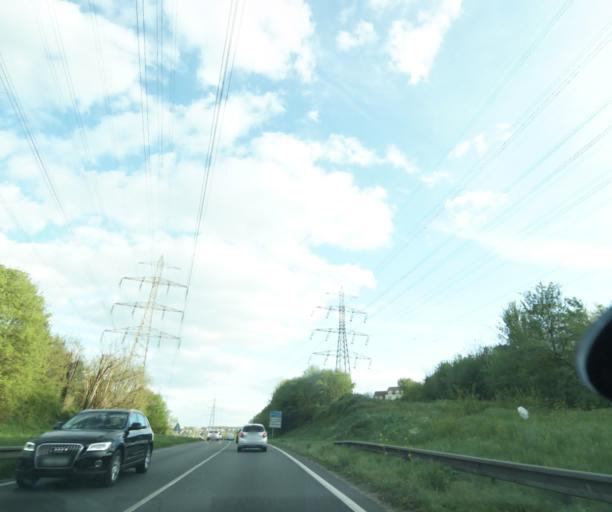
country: FR
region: Ile-de-France
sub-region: Departement de l'Essonne
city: Igny
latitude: 48.7413
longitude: 2.2243
